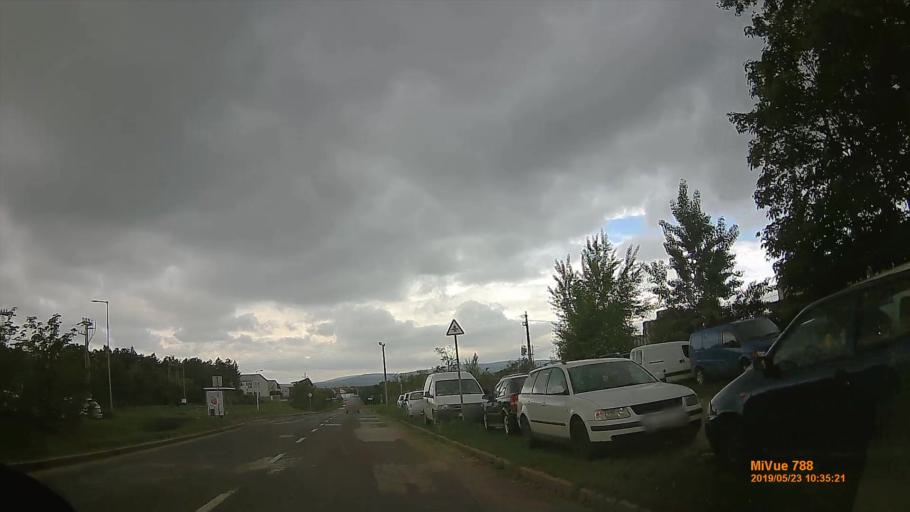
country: HU
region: Veszprem
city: Veszprem
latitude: 47.1087
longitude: 17.8915
